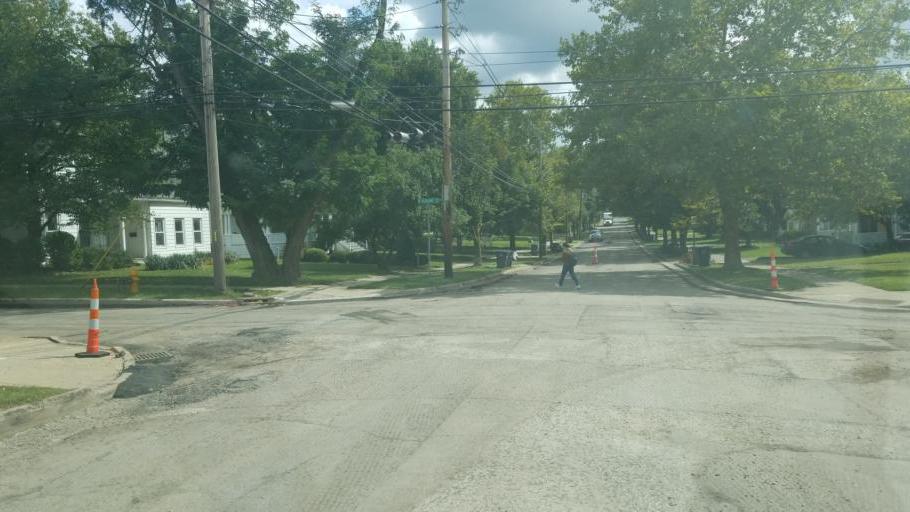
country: US
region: Ohio
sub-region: Lorain County
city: Oberlin
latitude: 41.2916
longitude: -82.2150
